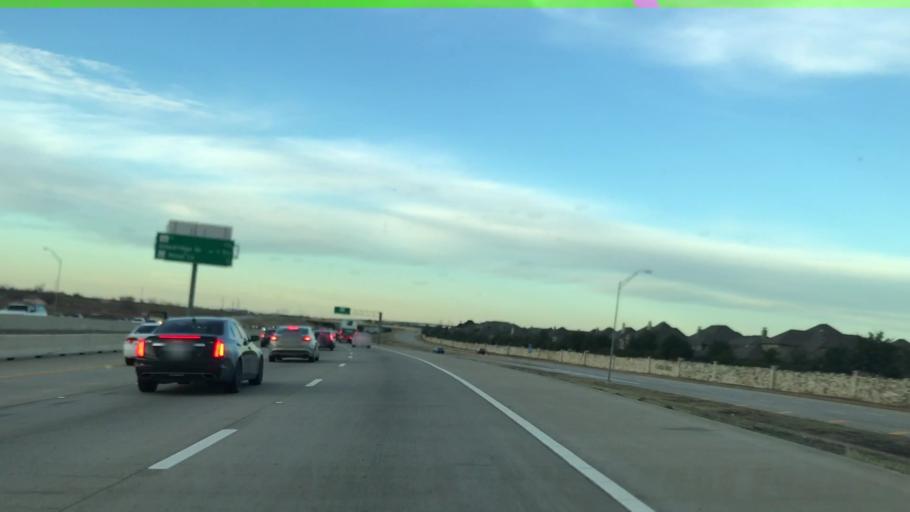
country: US
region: Texas
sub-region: Denton County
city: The Colony
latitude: 33.0397
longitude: -96.9226
